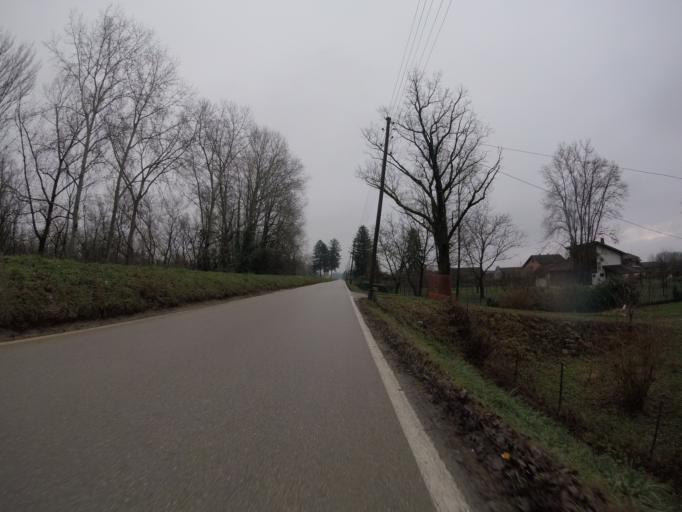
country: HR
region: Zagrebacka
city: Kuce
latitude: 45.6966
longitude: 16.2186
